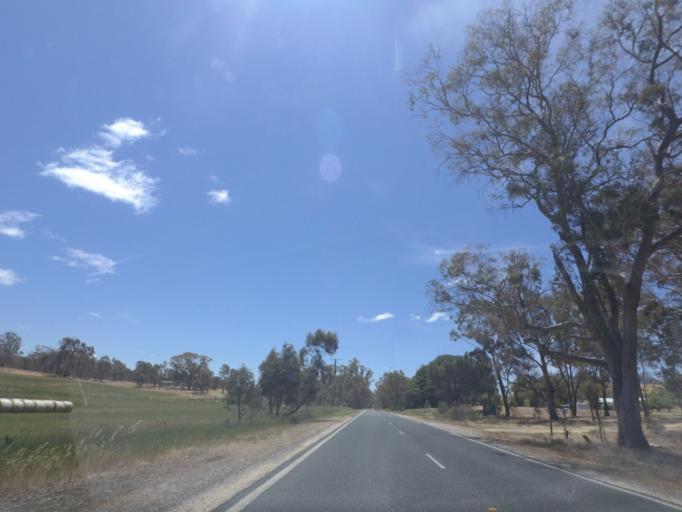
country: AU
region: Victoria
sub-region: Mount Alexander
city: Castlemaine
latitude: -37.1823
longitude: 144.1480
